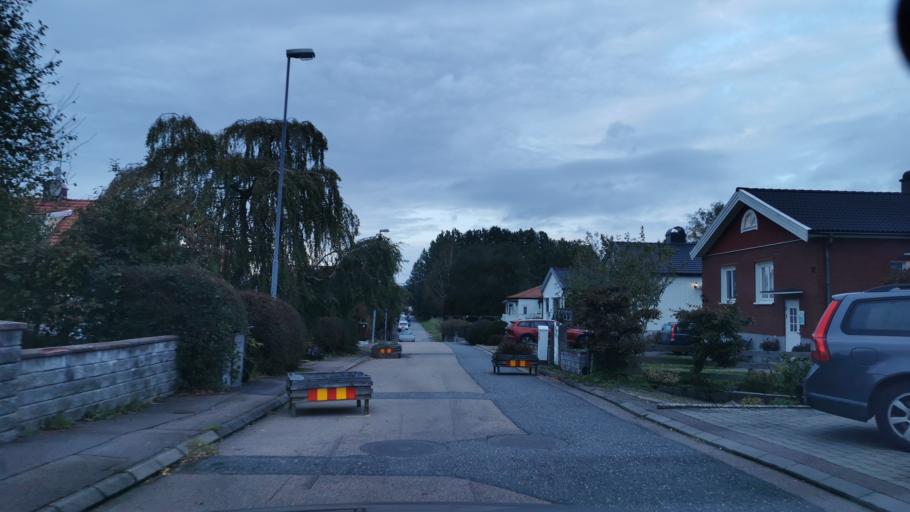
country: SE
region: Vaestra Goetaland
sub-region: Partille Kommun
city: Partille
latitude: 57.7275
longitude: 12.0924
